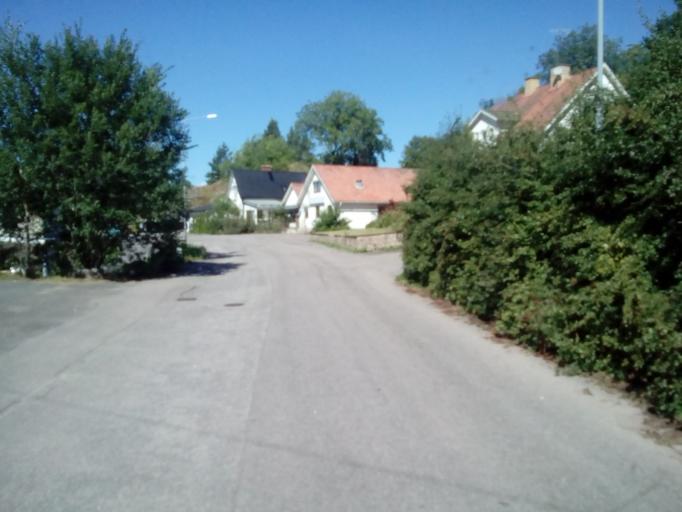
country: SE
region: OEstergoetland
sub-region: Kinda Kommun
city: Kisa
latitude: 57.9849
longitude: 15.6393
